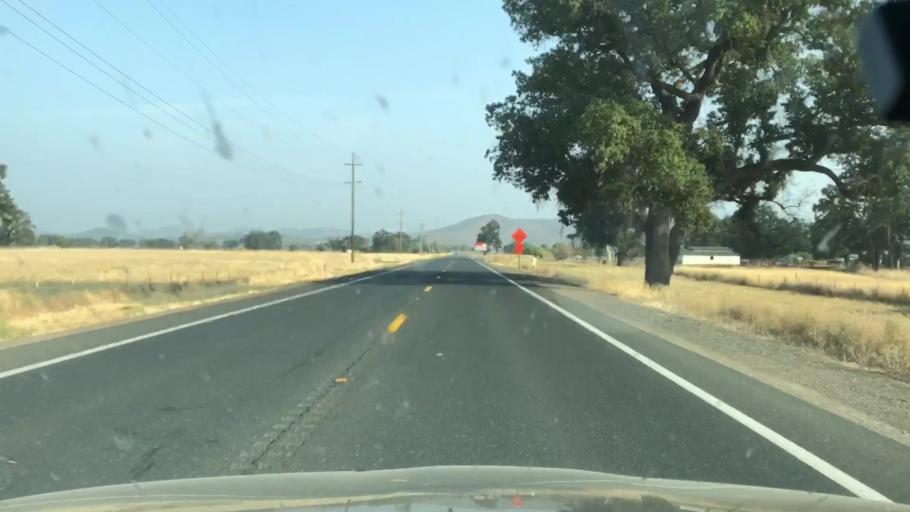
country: US
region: California
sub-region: Lake County
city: Hidden Valley Lake
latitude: 38.8010
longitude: -122.5715
